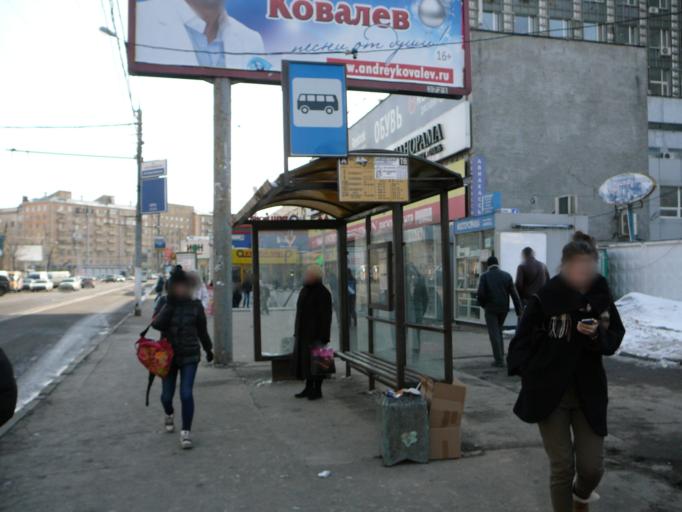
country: RU
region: Moskovskaya
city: Kozhukhovo
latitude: 55.7090
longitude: 37.6575
